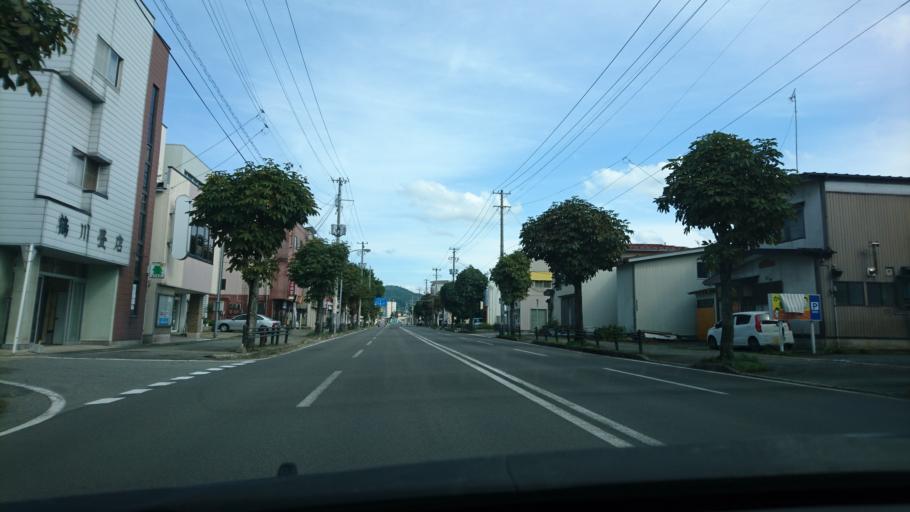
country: JP
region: Akita
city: Yokotemachi
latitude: 39.3100
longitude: 140.5658
